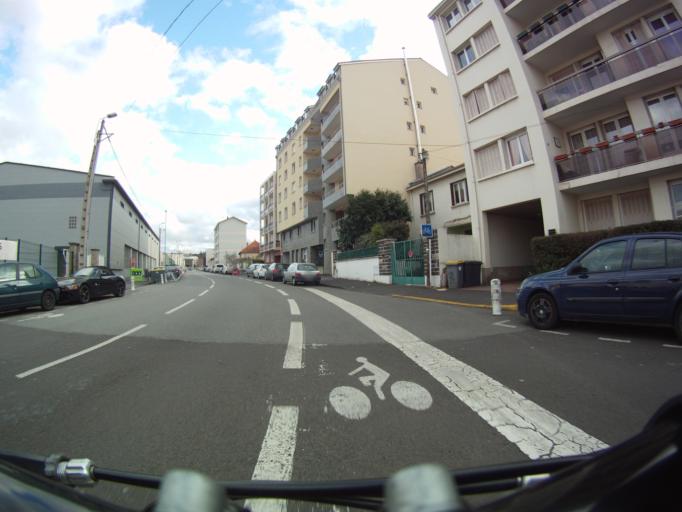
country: FR
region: Auvergne
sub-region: Departement du Puy-de-Dome
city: Beaumont
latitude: 45.7643
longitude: 3.0838
